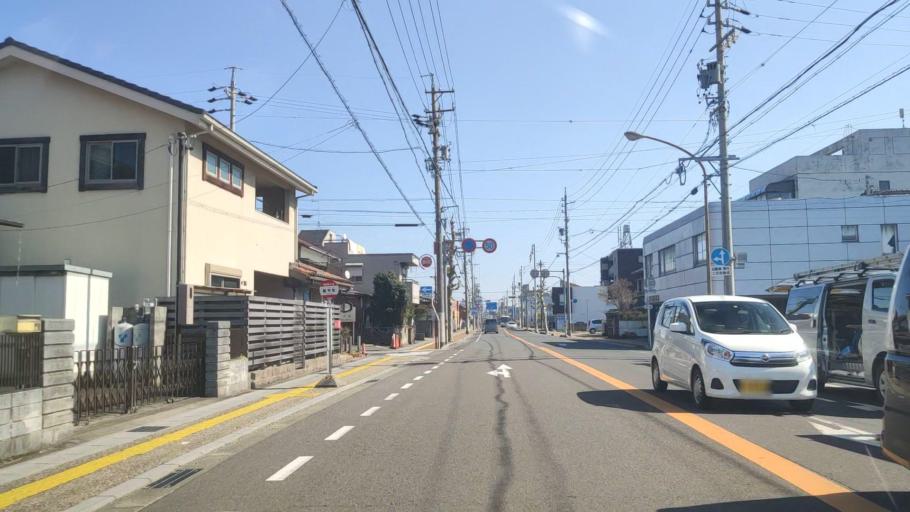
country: JP
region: Gifu
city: Gifu-shi
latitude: 35.3995
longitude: 136.7536
